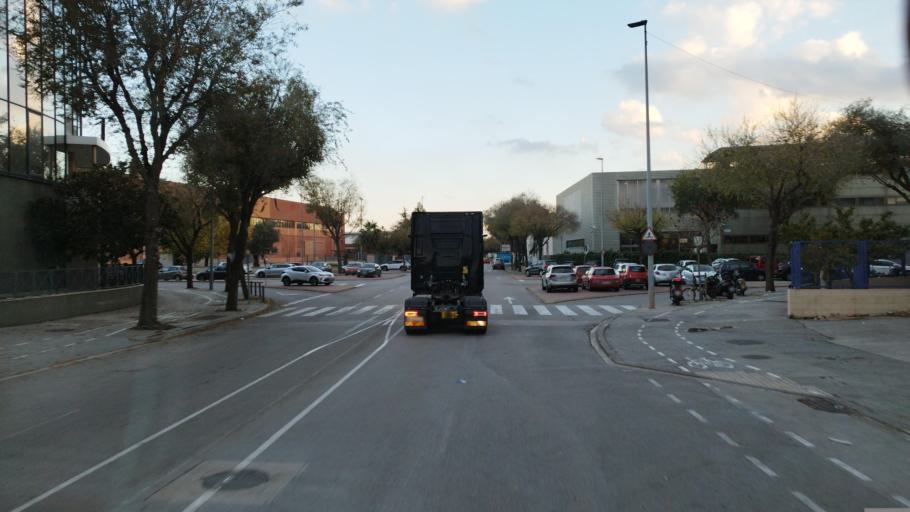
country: ES
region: Catalonia
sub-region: Provincia de Barcelona
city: L'Hospitalet de Llobregat
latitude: 41.3470
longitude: 2.1252
